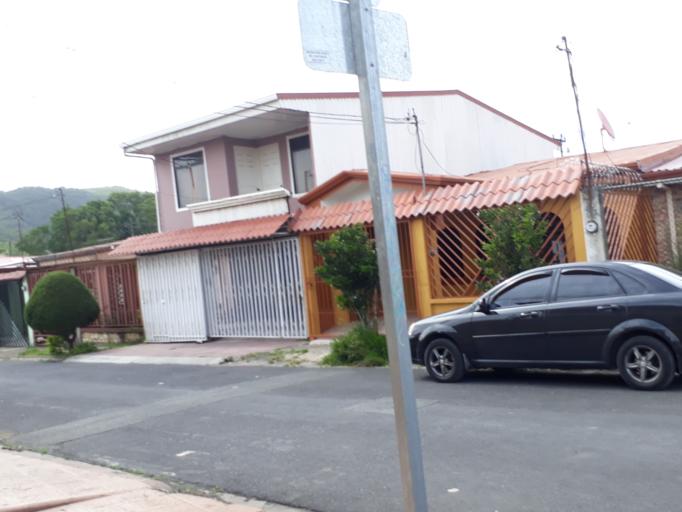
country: CR
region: Cartago
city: Cartago
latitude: 9.8751
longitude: -83.9407
